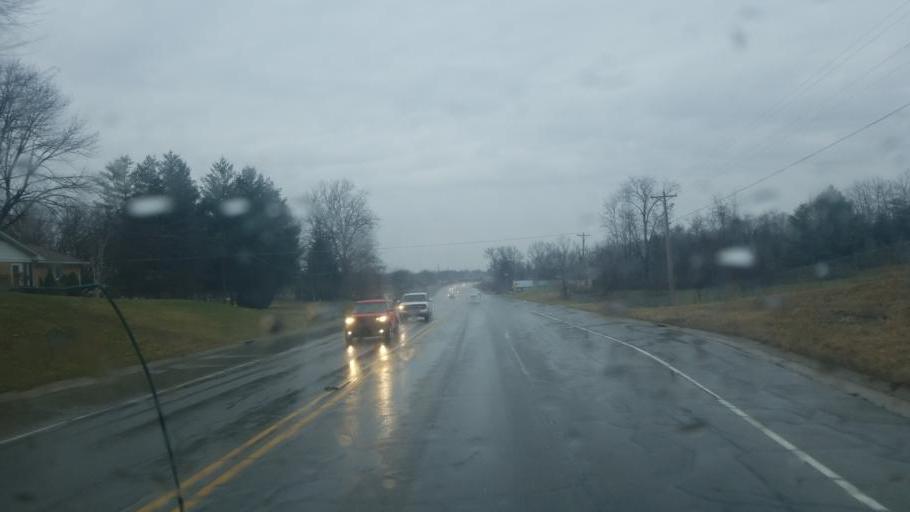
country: US
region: Indiana
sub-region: Bartholomew County
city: Columbus
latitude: 39.2062
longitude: -85.8689
